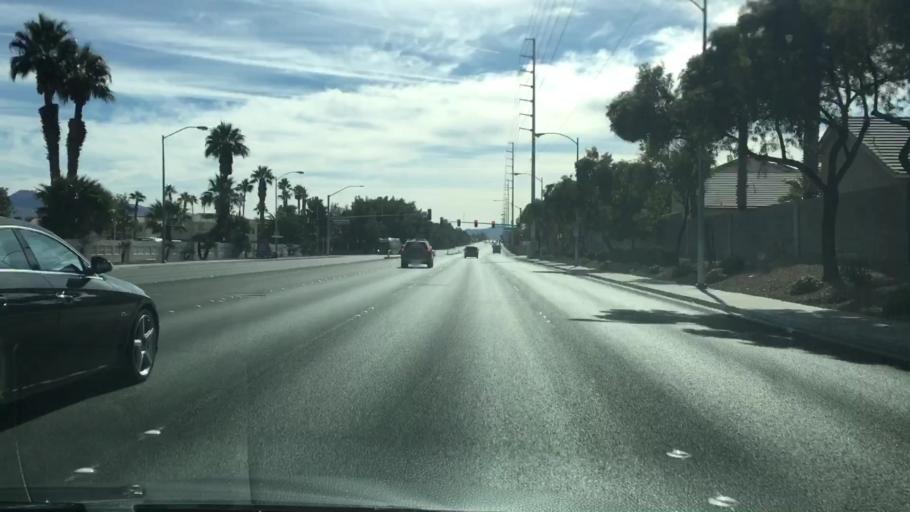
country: US
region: Nevada
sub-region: Clark County
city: Whitney
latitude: 36.0509
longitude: -115.1183
